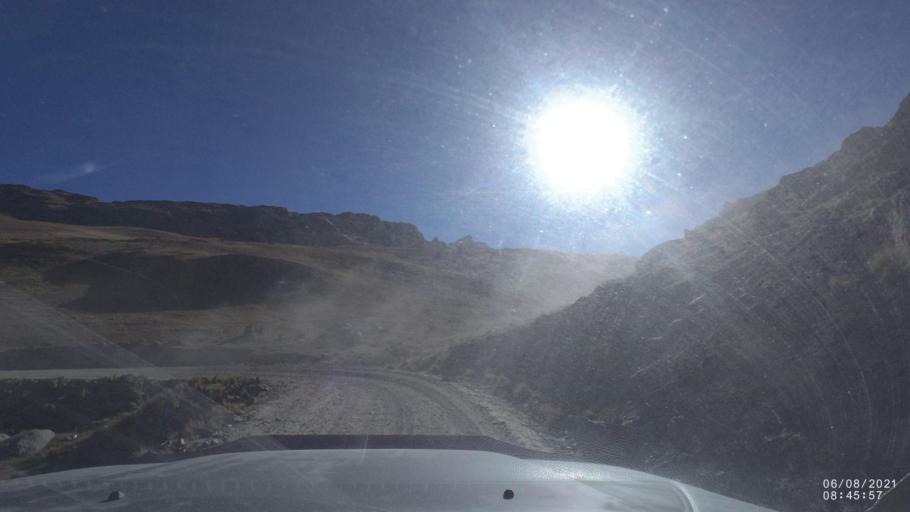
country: BO
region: Cochabamba
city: Sipe Sipe
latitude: -17.1692
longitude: -66.4177
